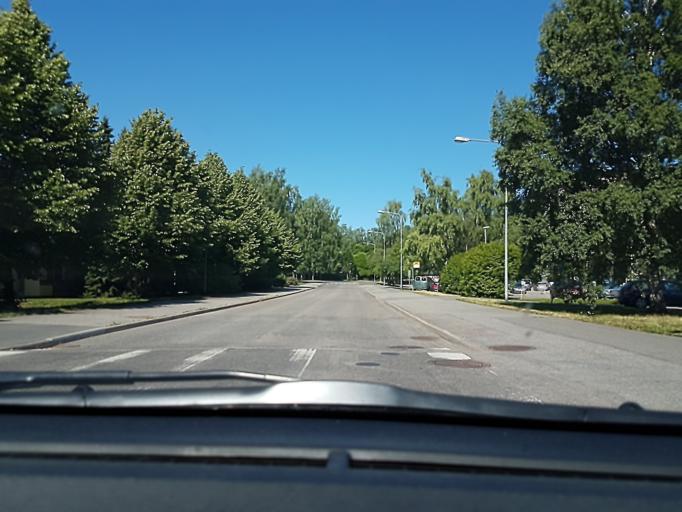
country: FI
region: Uusimaa
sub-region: Helsinki
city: Vantaa
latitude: 60.3129
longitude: 25.0349
